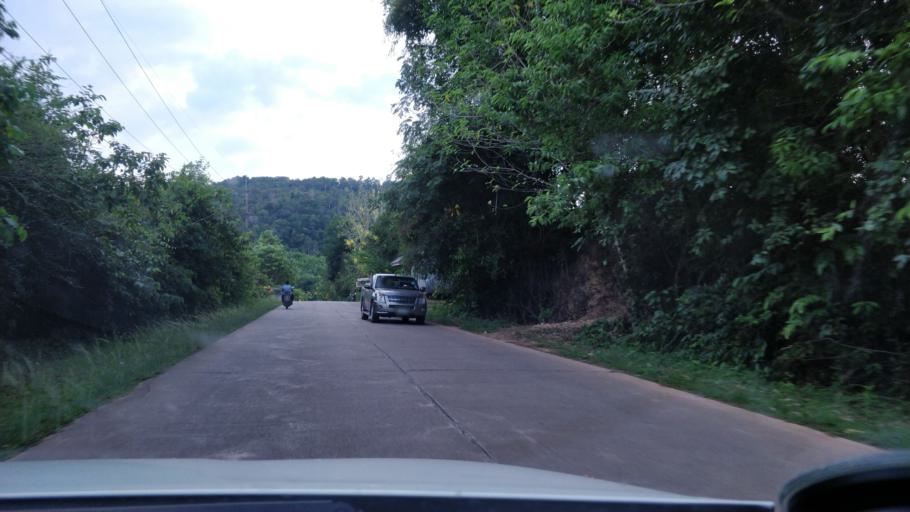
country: TH
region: Krabi
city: Saladan
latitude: 7.5850
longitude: 99.0684
